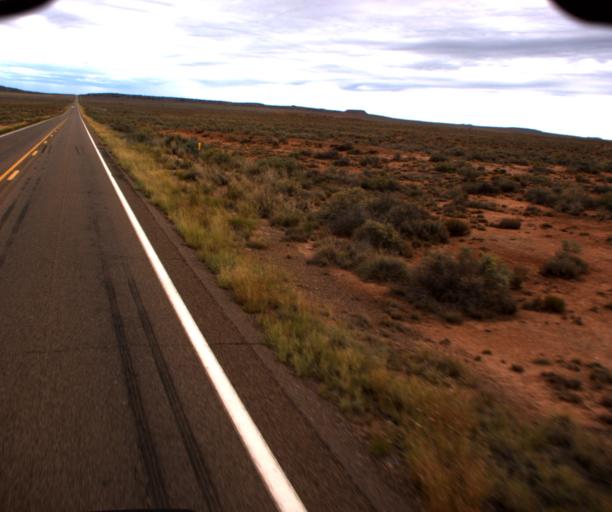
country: US
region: Arizona
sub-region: Navajo County
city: Holbrook
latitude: 34.7346
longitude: -110.1178
